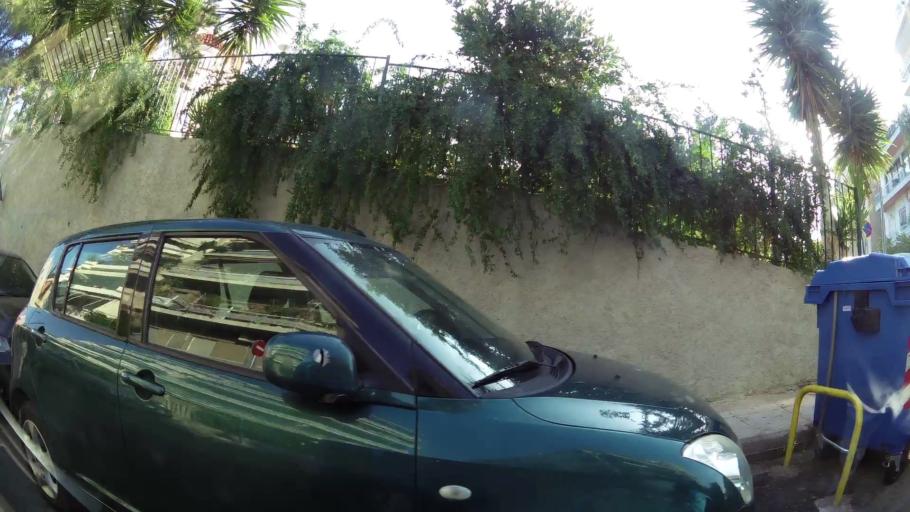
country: GR
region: Attica
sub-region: Nomarchia Athinas
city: Kaisariani
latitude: 37.9764
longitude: 23.7632
